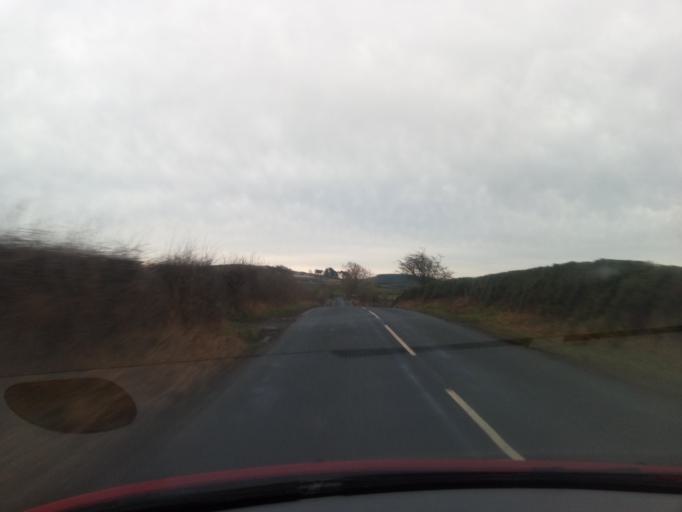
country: GB
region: England
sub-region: Northumberland
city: Ellingham
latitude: 55.4596
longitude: -1.7808
